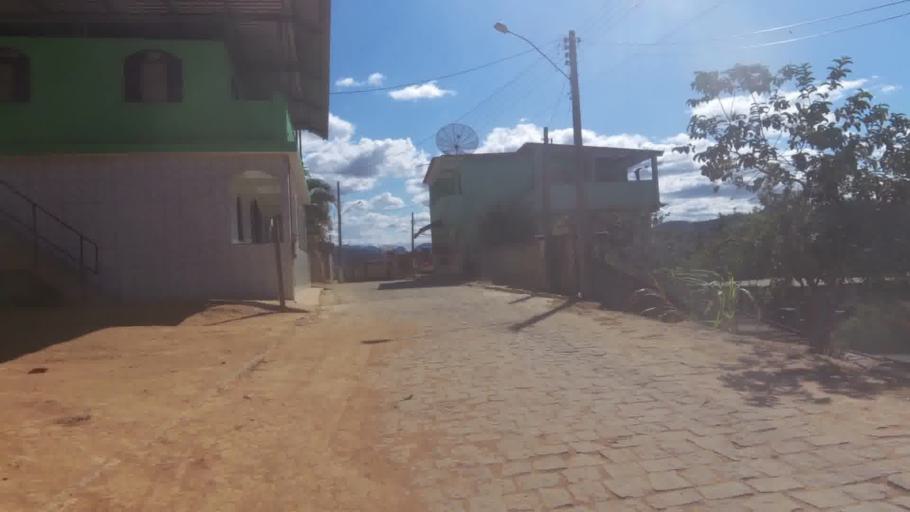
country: BR
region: Espirito Santo
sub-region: Cachoeiro De Itapemirim
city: Cachoeiro de Itapemirim
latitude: -20.9178
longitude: -41.1949
